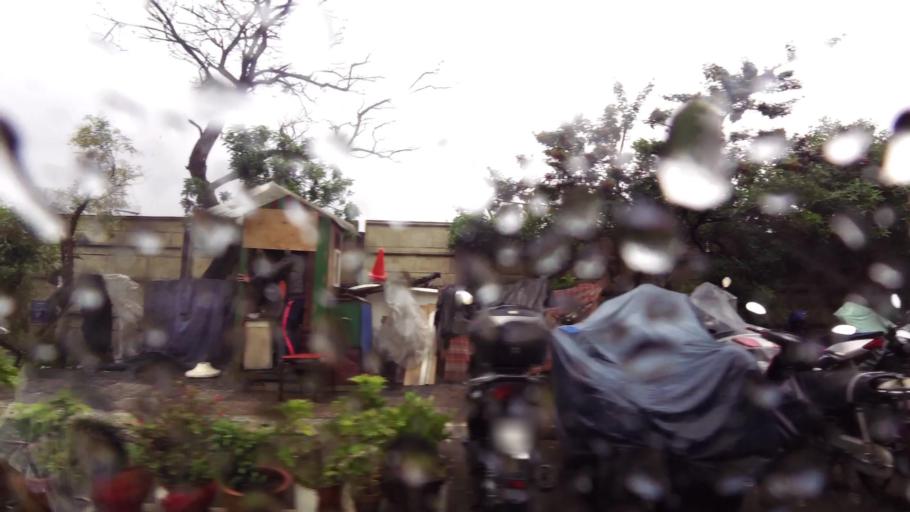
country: MA
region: Grand Casablanca
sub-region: Casablanca
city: Casablanca
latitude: 33.5567
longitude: -7.6682
